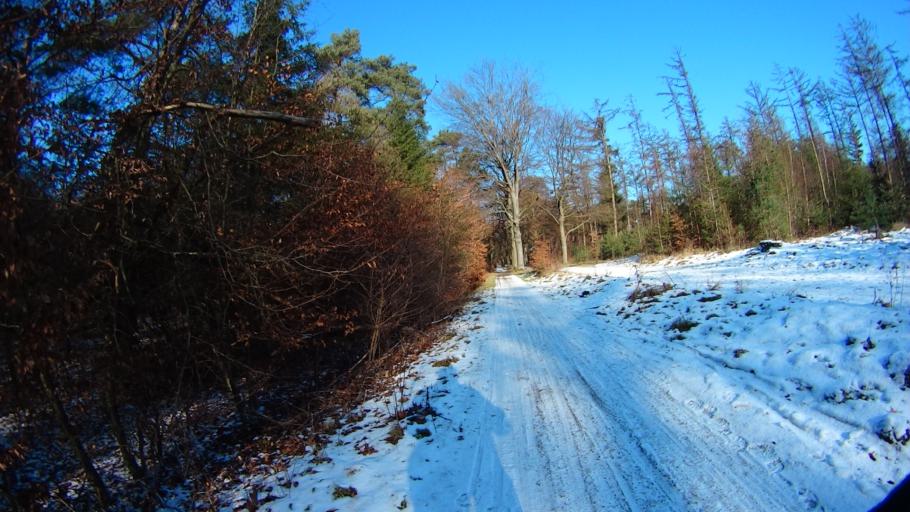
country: NL
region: North Holland
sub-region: Gemeente Hilversum
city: Hilversum
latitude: 52.2076
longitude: 5.2170
